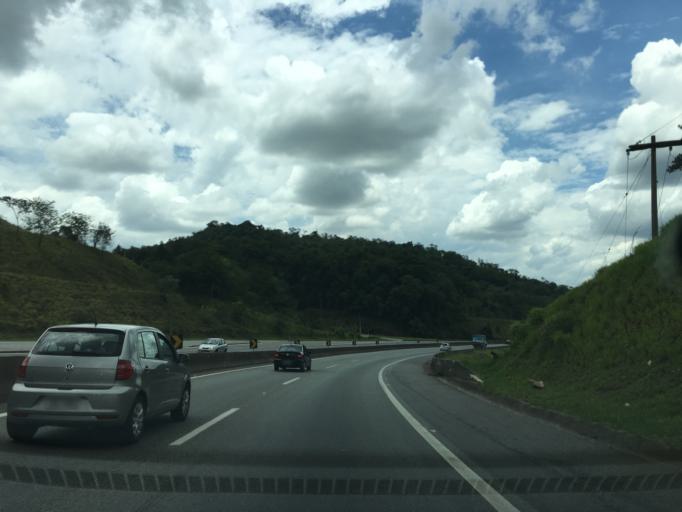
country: BR
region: Sao Paulo
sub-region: Mairipora
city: Mairipora
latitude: -23.2337
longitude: -46.6020
